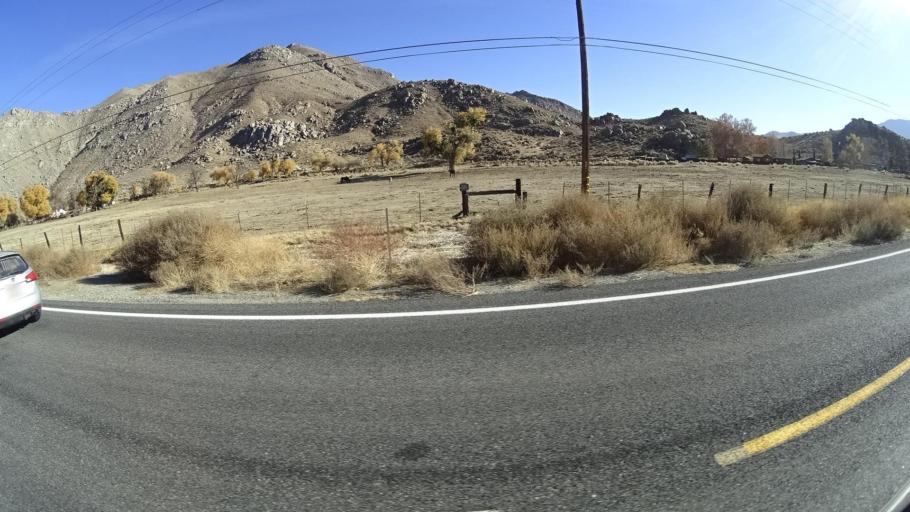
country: US
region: California
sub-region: Kern County
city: Weldon
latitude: 35.6726
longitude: -118.2603
